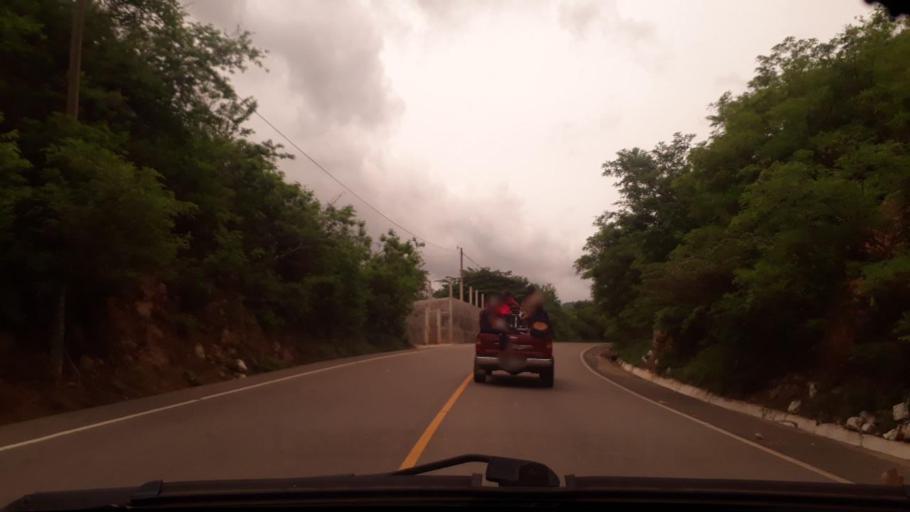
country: GT
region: Chiquimula
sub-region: Municipio de Camotan
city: Camotan
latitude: 14.8221
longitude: -89.3611
